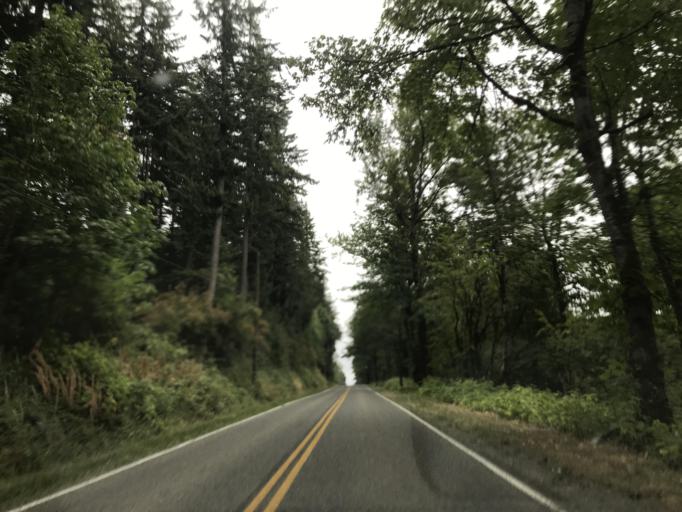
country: US
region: Washington
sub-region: Whatcom County
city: Sudden Valley
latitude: 48.7839
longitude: -122.3331
